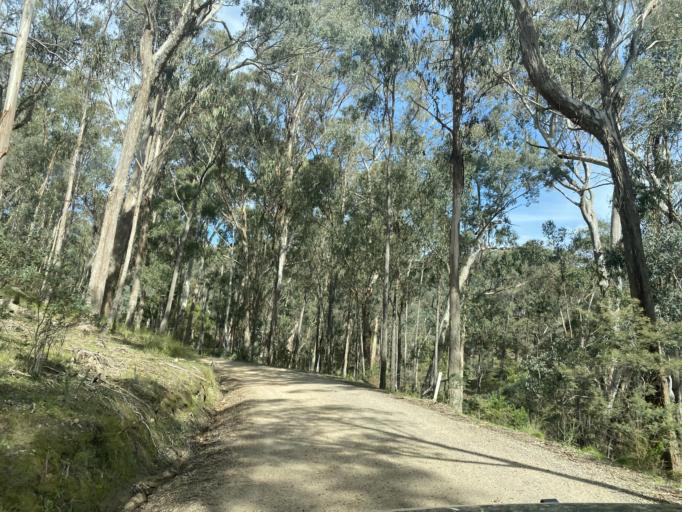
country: AU
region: Victoria
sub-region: Mansfield
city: Mansfield
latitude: -36.8235
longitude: 146.1520
